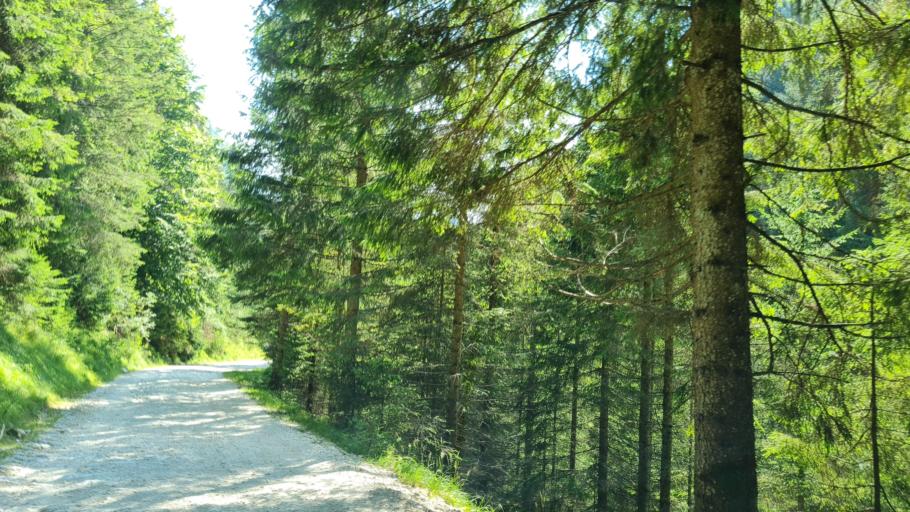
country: IT
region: Veneto
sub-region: Provincia di Vicenza
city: Roana
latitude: 45.9174
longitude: 11.4747
